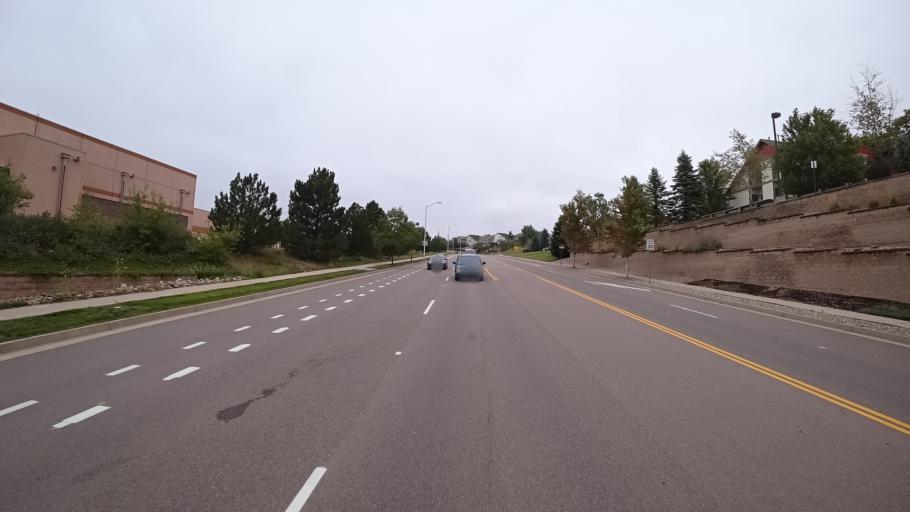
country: US
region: Colorado
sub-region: El Paso County
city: Cimarron Hills
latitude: 38.8960
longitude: -104.7163
